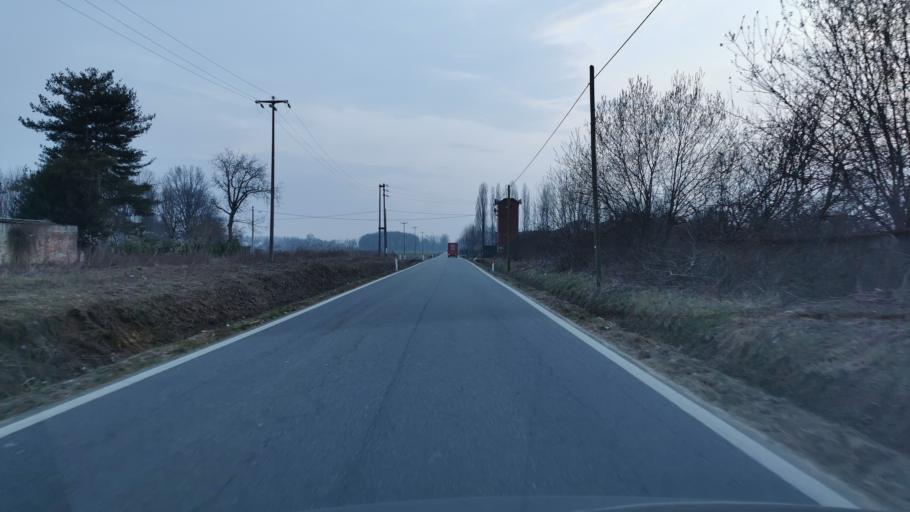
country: IT
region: Piedmont
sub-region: Provincia di Torino
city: Montalenghe
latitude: 45.3257
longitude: 7.8322
